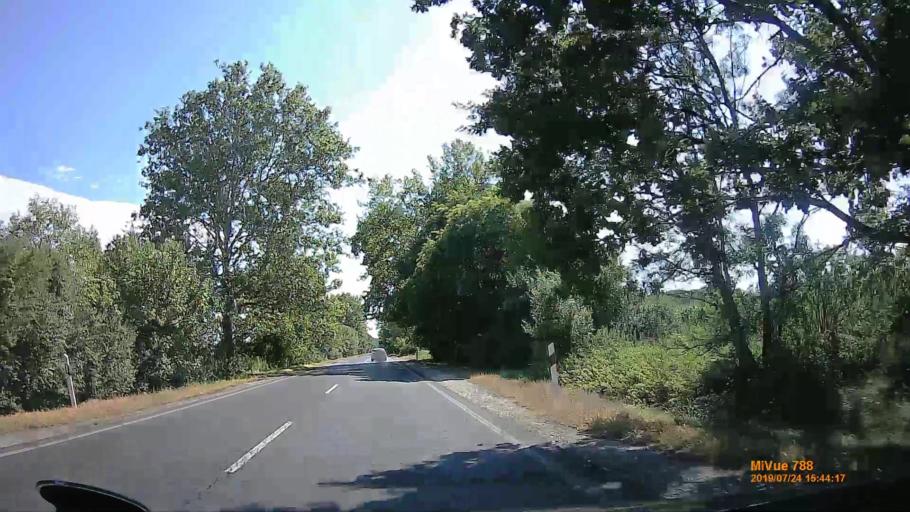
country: HU
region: Szabolcs-Szatmar-Bereg
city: Vasarosnameny
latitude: 48.1018
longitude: 22.2964
